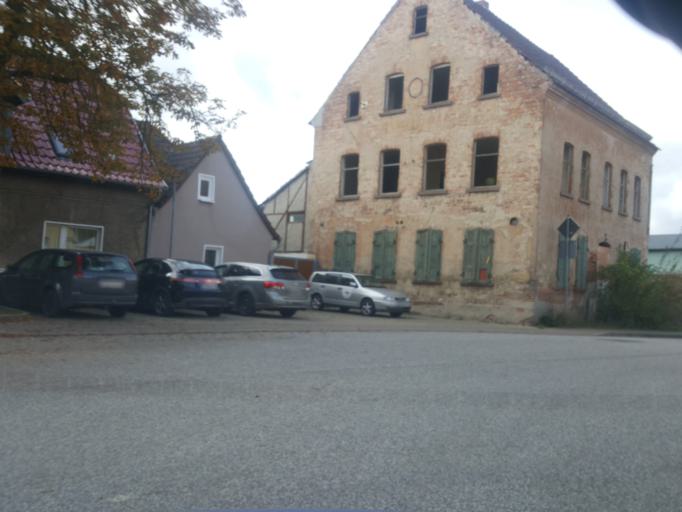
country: DE
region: Saxony-Anhalt
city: Riestedt
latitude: 51.4951
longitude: 11.3634
